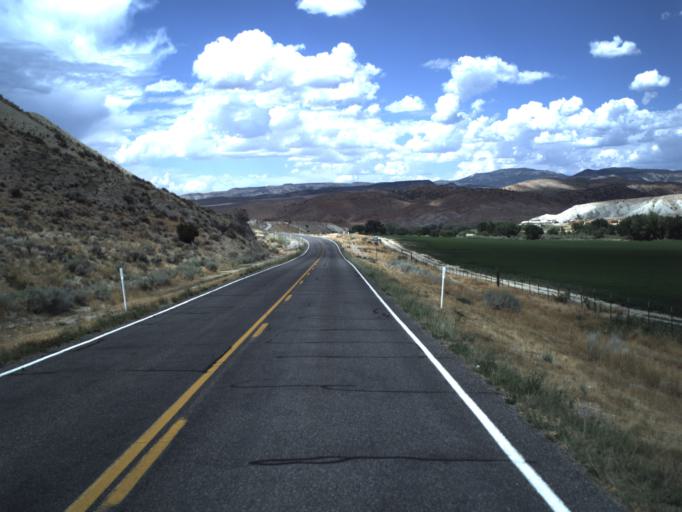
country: US
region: Utah
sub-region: Sanpete County
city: Centerfield
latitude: 39.1378
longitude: -111.7308
